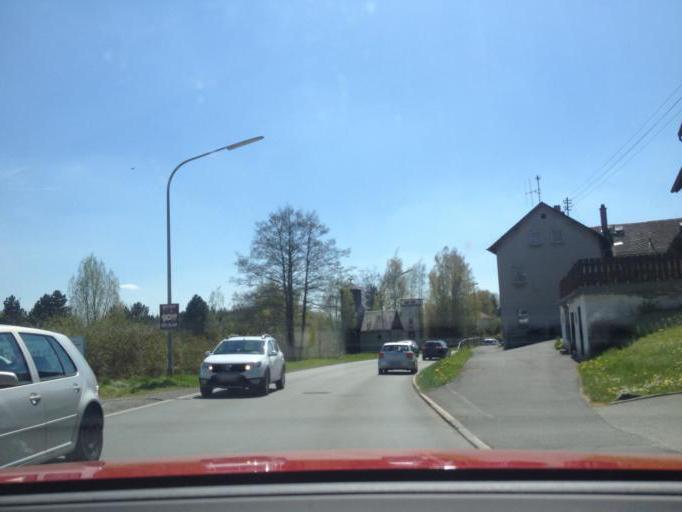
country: DE
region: Bavaria
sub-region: Upper Franconia
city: Oberkotzau
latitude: 50.2457
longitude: 11.9364
